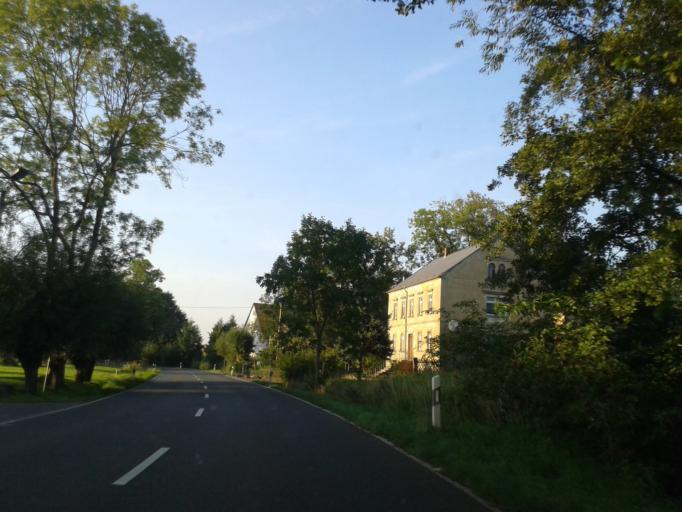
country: DE
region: Saxony
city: Klipphausen
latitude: 51.1063
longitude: 13.4875
